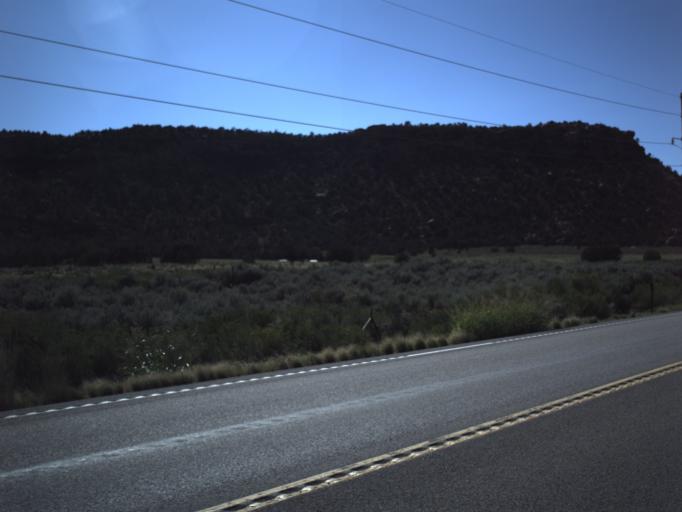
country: US
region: Utah
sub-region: Washington County
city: LaVerkin
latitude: 37.1116
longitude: -113.1483
